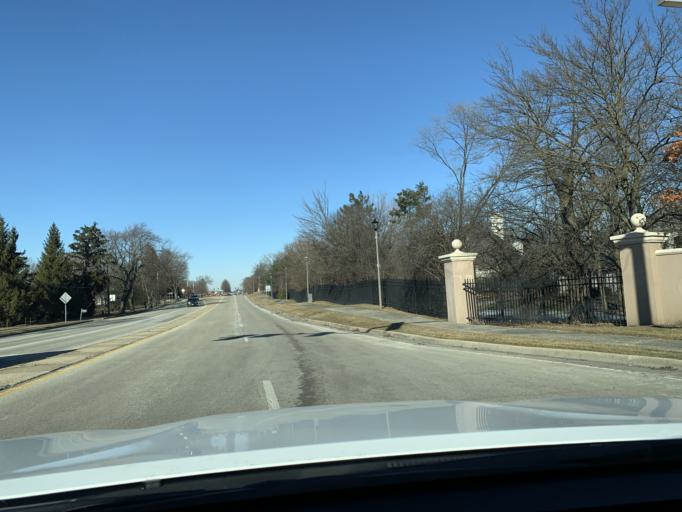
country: US
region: Illinois
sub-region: DuPage County
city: Burr Ridge
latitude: 41.7459
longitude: -87.9153
